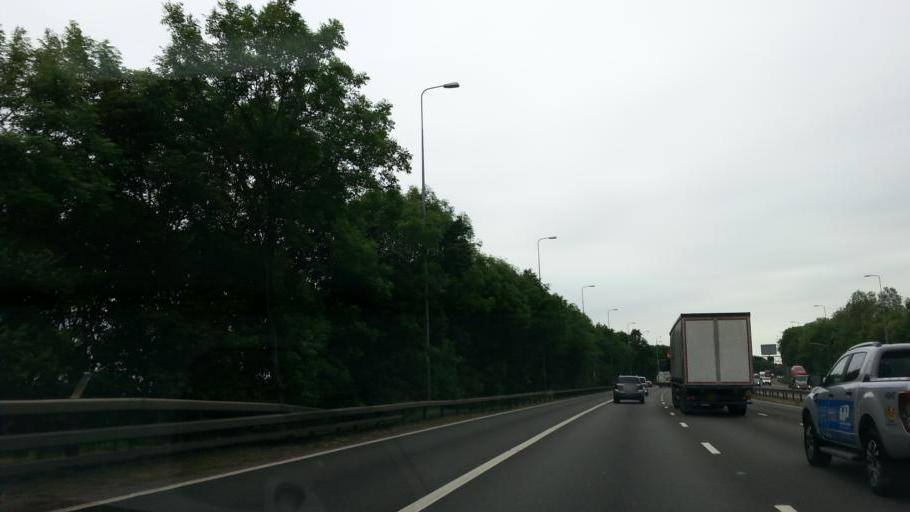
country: GB
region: England
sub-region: Solihull
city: Knowle
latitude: 52.4108
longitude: -1.7304
